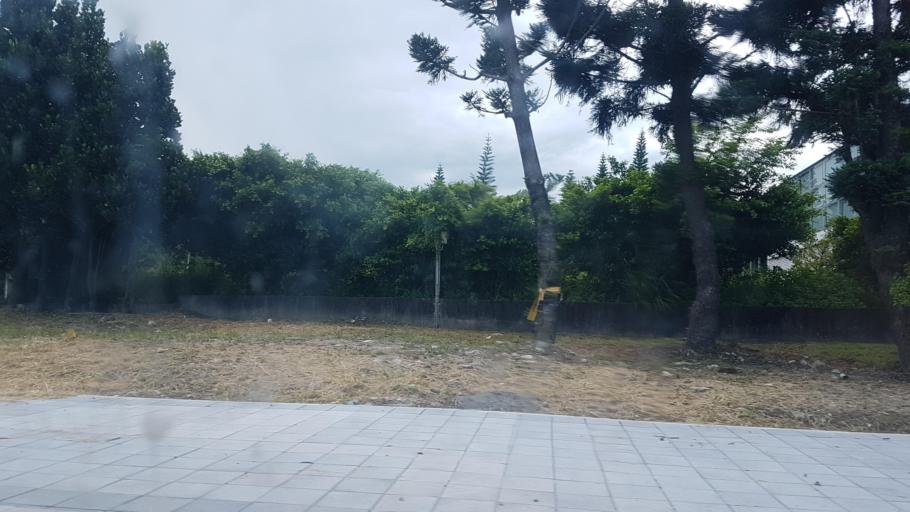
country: TW
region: Taiwan
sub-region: Hualien
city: Hualian
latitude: 23.9275
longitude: 121.5918
